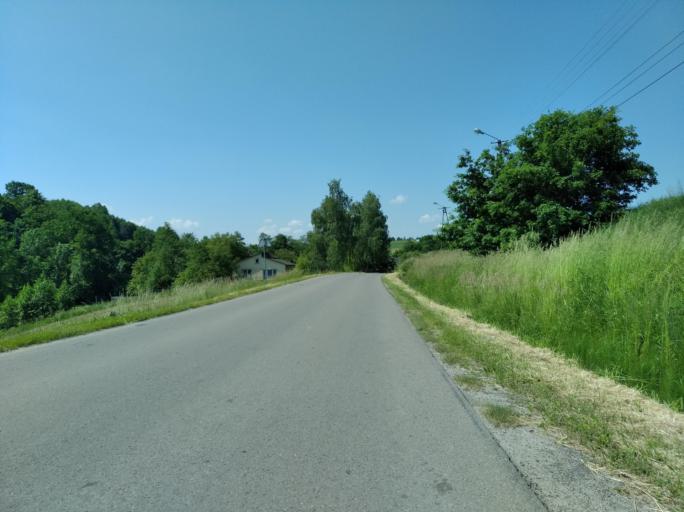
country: PL
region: Subcarpathian Voivodeship
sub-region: Powiat ropczycko-sedziszowski
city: Zagorzyce
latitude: 50.0039
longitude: 21.6562
